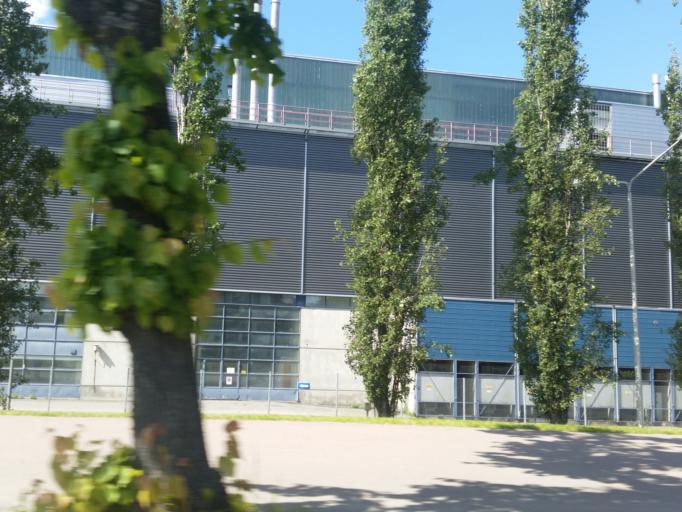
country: FI
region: Northern Savo
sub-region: Varkaus
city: Varkaus
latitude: 62.3158
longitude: 27.8914
